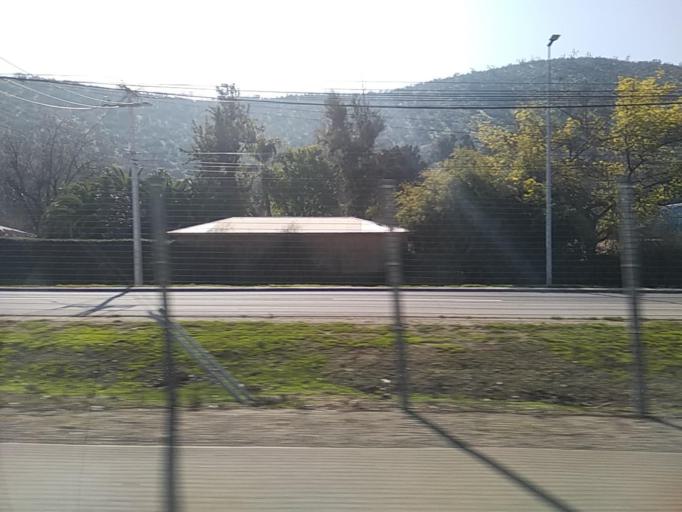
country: CL
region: Santiago Metropolitan
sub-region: Provincia de Chacabuco
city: Lampa
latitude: -33.4124
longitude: -71.0557
